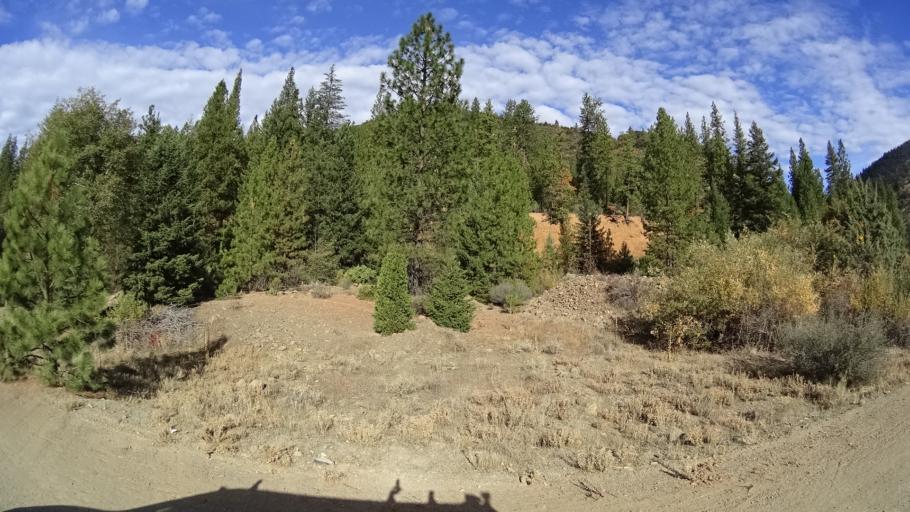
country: US
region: California
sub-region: Siskiyou County
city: Yreka
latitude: 41.7125
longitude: -122.8058
